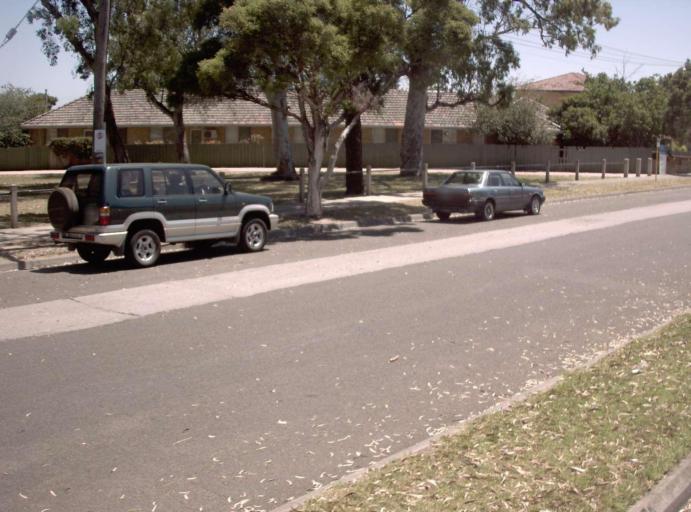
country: AU
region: Victoria
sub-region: Greater Dandenong
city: Dandenong
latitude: -37.9795
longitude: 145.2081
